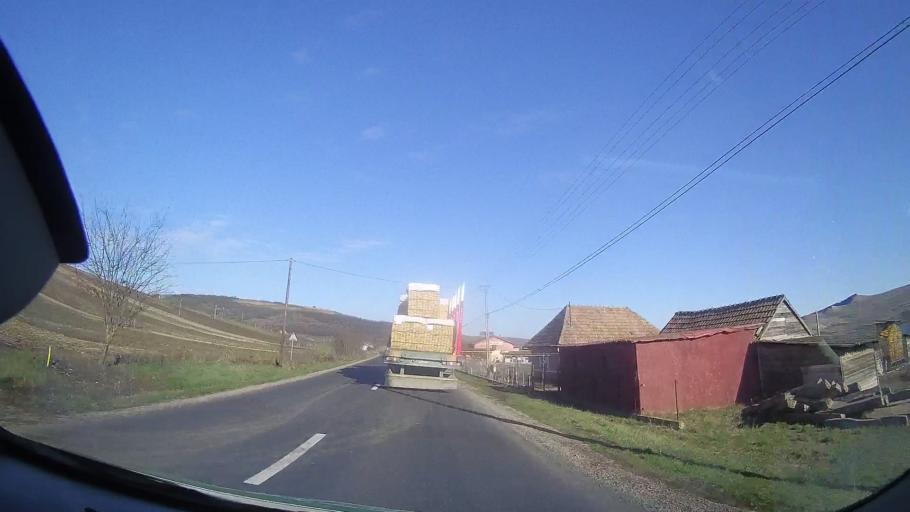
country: RO
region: Mures
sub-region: Comuna Zau De Campie
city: Zau de Campie
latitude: 46.6318
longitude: 24.1328
